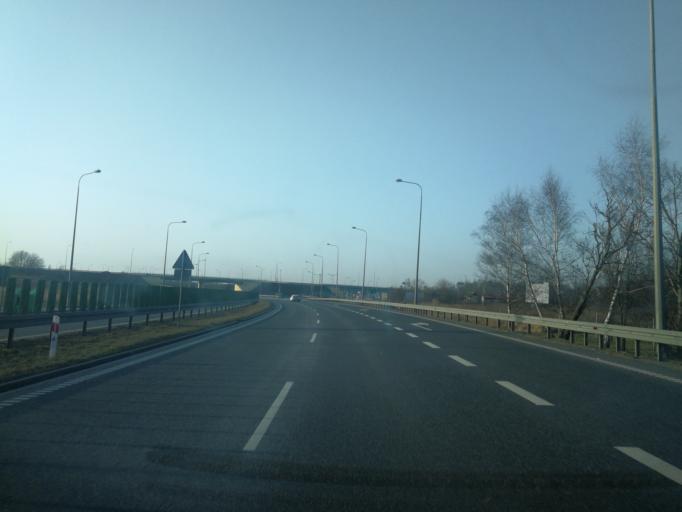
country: PL
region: Warmian-Masurian Voivodeship
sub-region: Powiat elblaski
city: Gronowo Gorne
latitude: 54.1359
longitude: 19.4537
